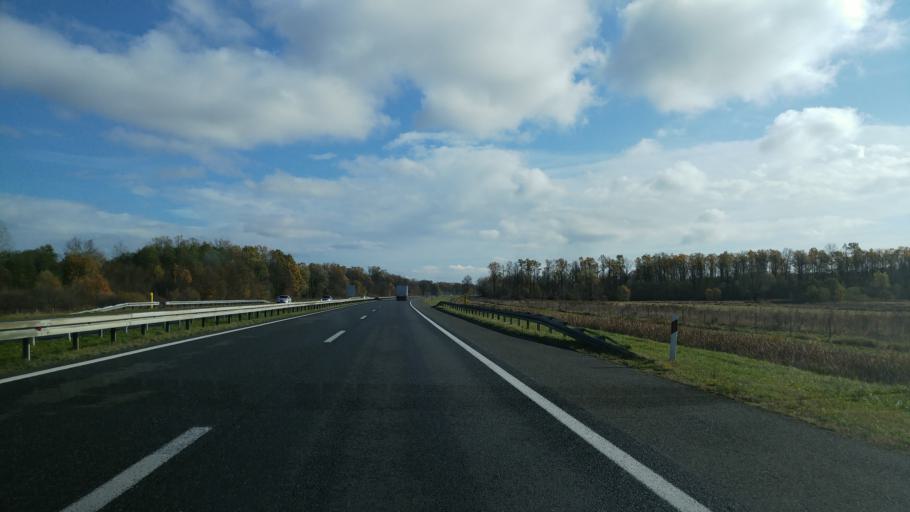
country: HR
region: Zagrebacka
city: Lupoglav
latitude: 45.7488
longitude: 16.3093
